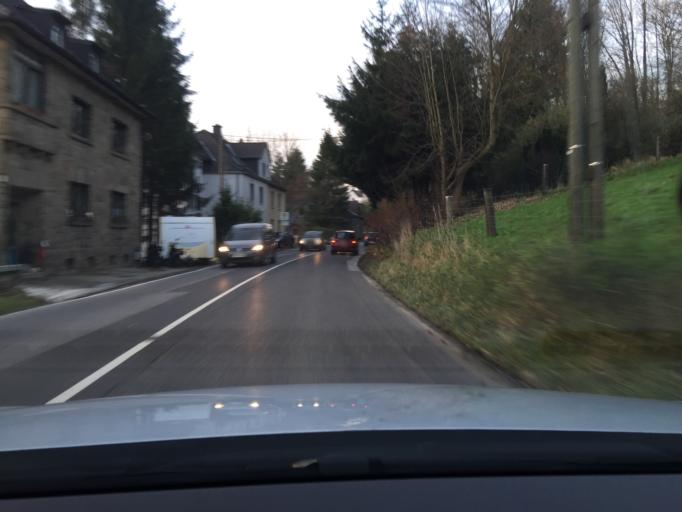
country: DE
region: North Rhine-Westphalia
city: Hattingen
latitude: 51.3790
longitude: 7.1253
